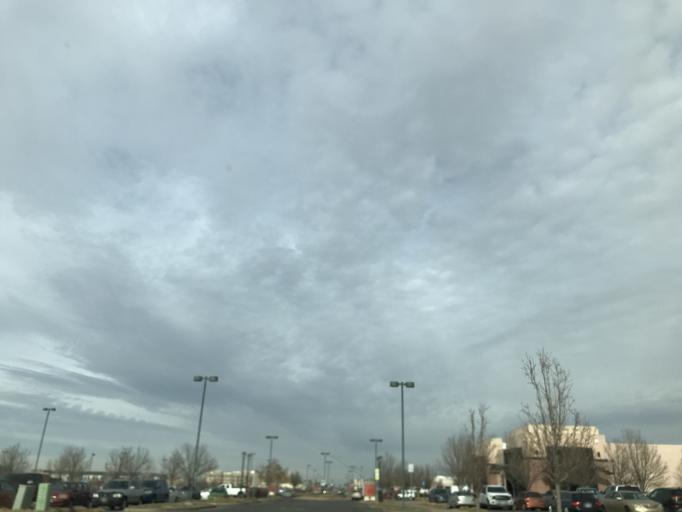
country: US
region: Colorado
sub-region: Adams County
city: Commerce City
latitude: 39.7815
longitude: -104.8933
